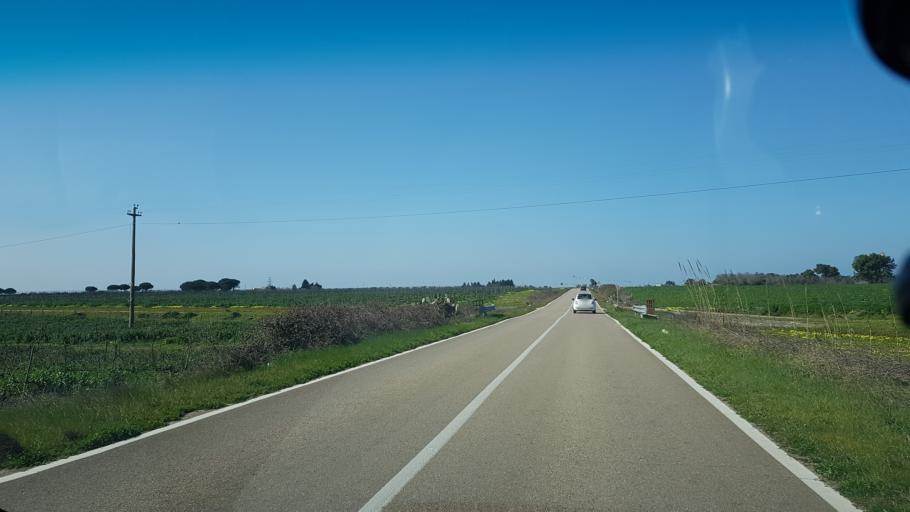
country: IT
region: Apulia
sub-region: Provincia di Brindisi
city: Torchiarolo
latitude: 40.5325
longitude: 18.0640
